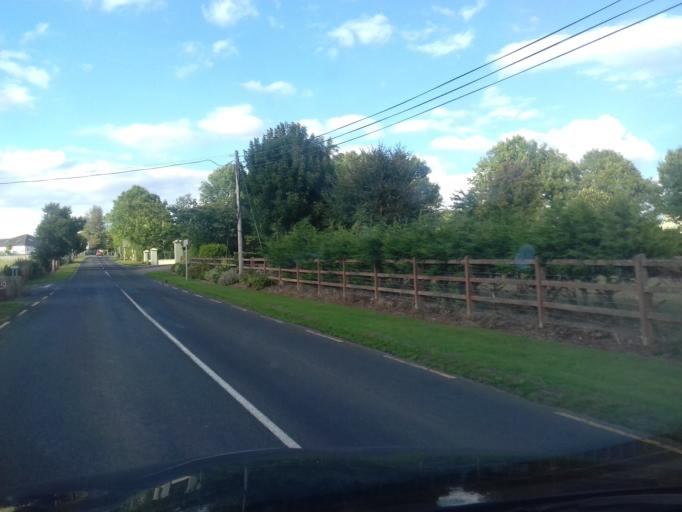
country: IE
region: Leinster
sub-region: Loch Garman
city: New Ross
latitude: 52.4505
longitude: -6.9626
